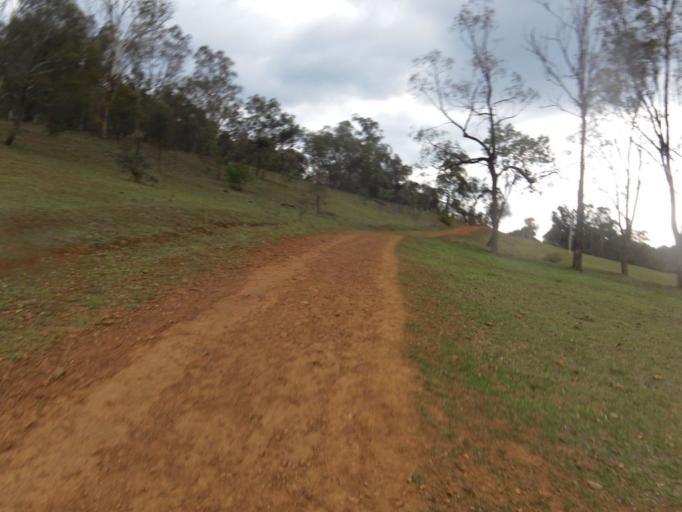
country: AU
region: Australian Capital Territory
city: Forrest
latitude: -35.3325
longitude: 149.1204
